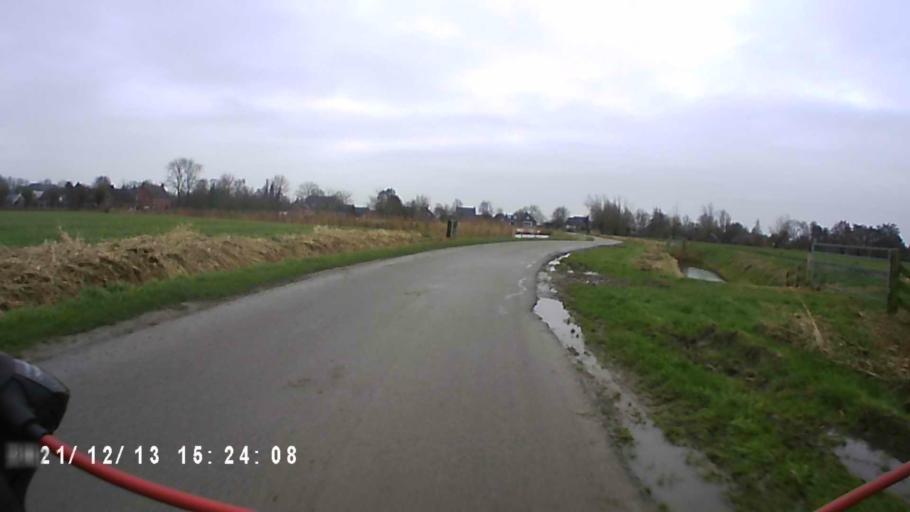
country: NL
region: Groningen
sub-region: Gemeente Appingedam
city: Appingedam
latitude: 53.3435
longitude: 6.7953
